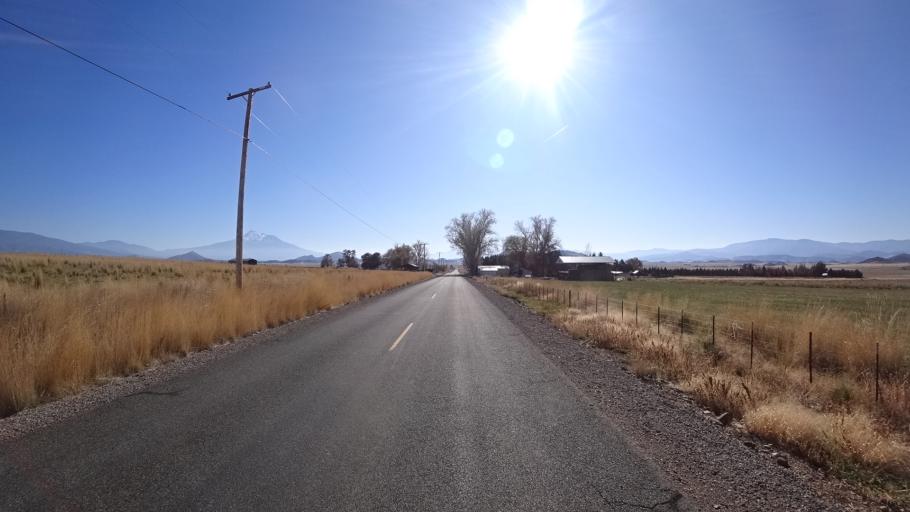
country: US
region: California
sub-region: Siskiyou County
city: Montague
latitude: 41.7352
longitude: -122.4574
